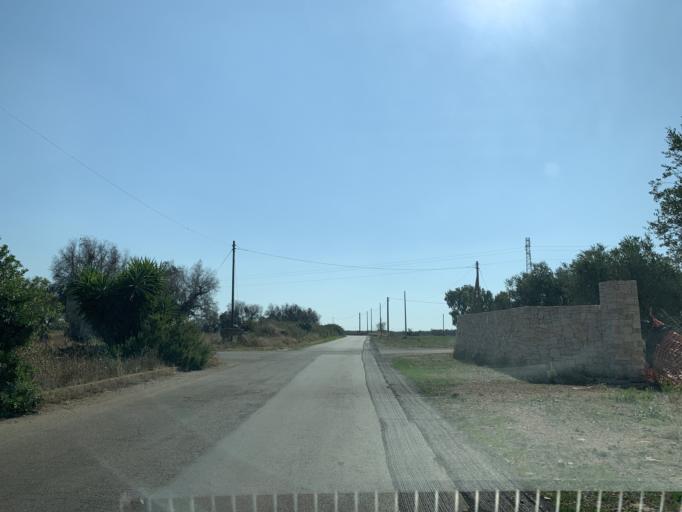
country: IT
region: Apulia
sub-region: Provincia di Lecce
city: Copertino
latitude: 40.2627
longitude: 18.0282
